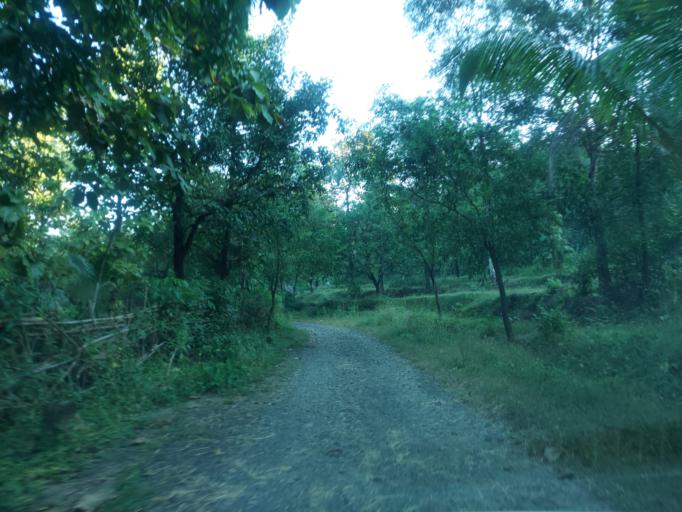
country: IN
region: Maharashtra
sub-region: Sindhudurg
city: Kudal
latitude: 16.0704
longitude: 73.8248
